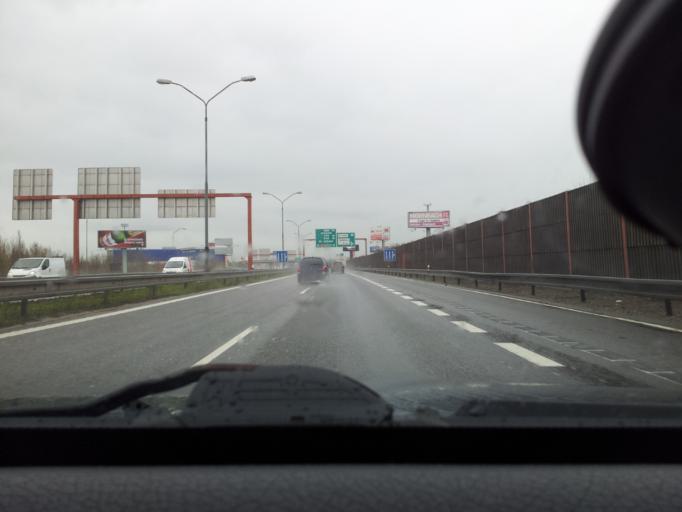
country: SK
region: Bratislavsky
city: Svaty Jur
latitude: 48.1758
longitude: 17.1892
